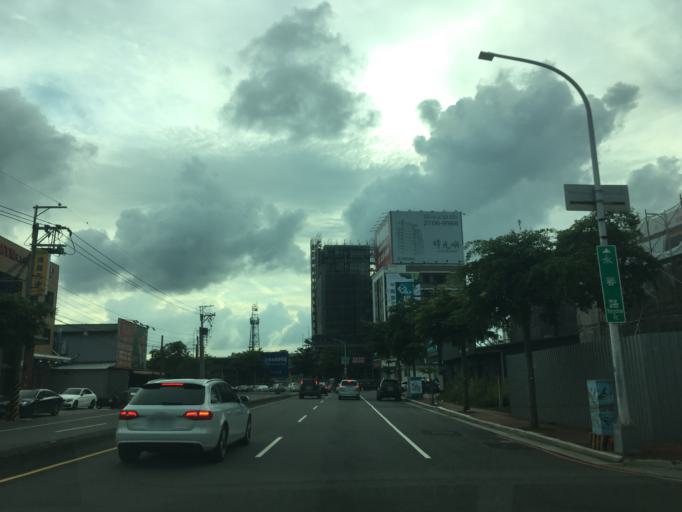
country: TW
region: Taiwan
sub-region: Taichung City
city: Taichung
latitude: 24.1407
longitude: 120.6253
